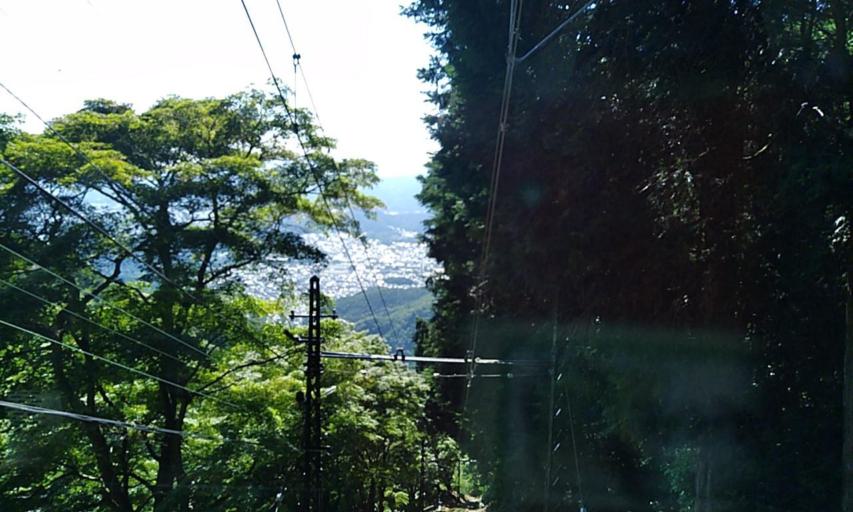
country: JP
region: Kyoto
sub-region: Kyoto-shi
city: Kamigyo-ku
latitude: 35.0647
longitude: 135.8192
